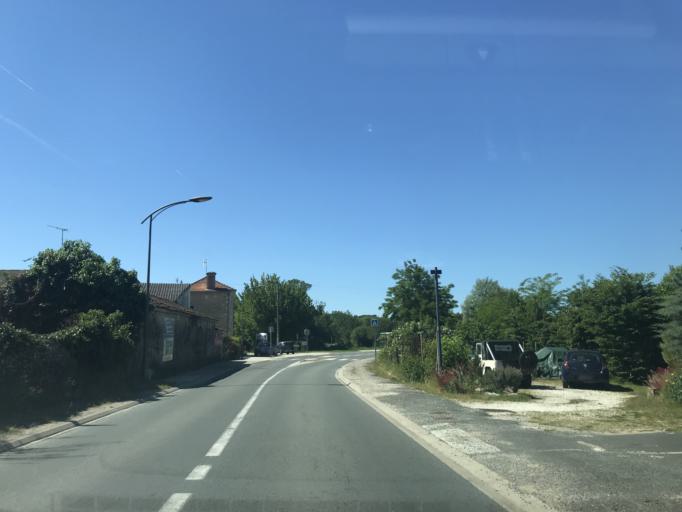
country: FR
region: Poitou-Charentes
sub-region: Departement de la Charente-Maritime
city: Gemozac
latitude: 45.5657
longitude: -0.7200
